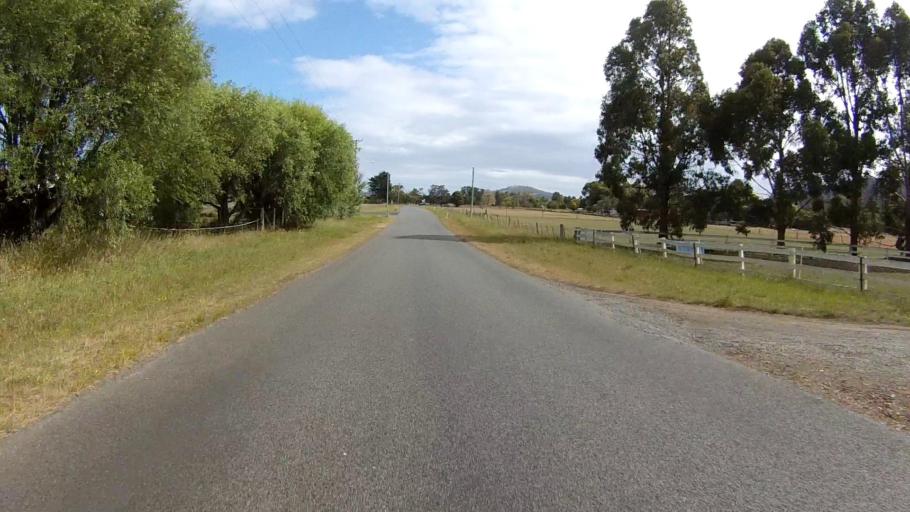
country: AU
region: Tasmania
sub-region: Clarence
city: Acton Park
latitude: -42.8873
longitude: 147.4965
